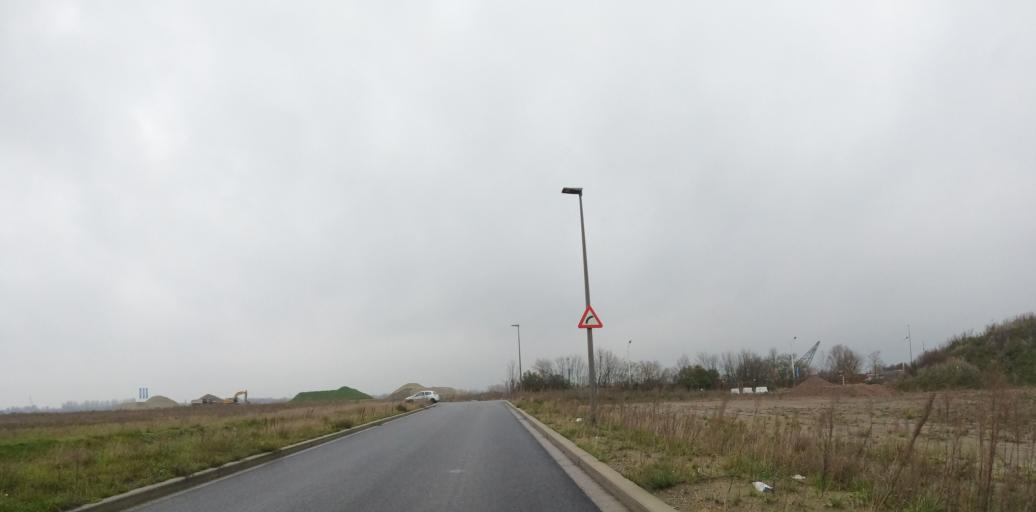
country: BE
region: Flanders
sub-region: Provincie Antwerpen
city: Hoboken
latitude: 51.2005
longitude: 4.3673
